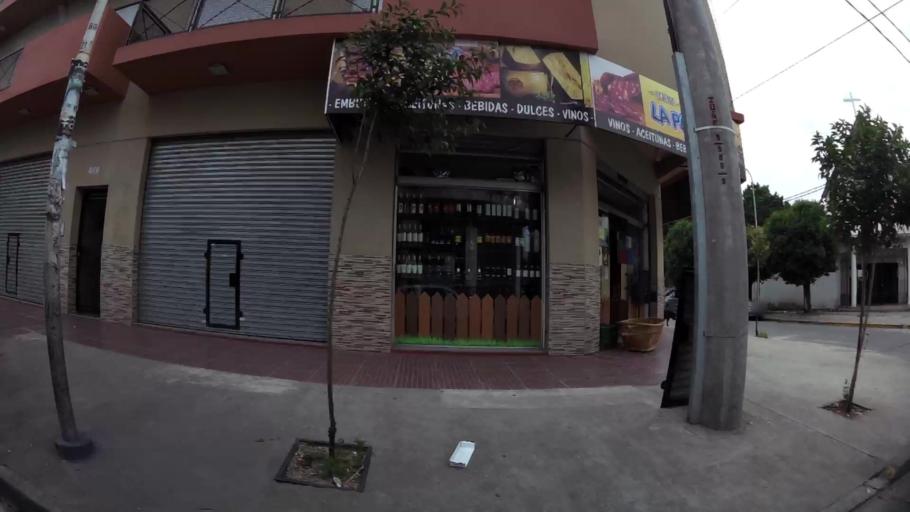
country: AR
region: Buenos Aires
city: San Justo
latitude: -34.6986
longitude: -58.5277
